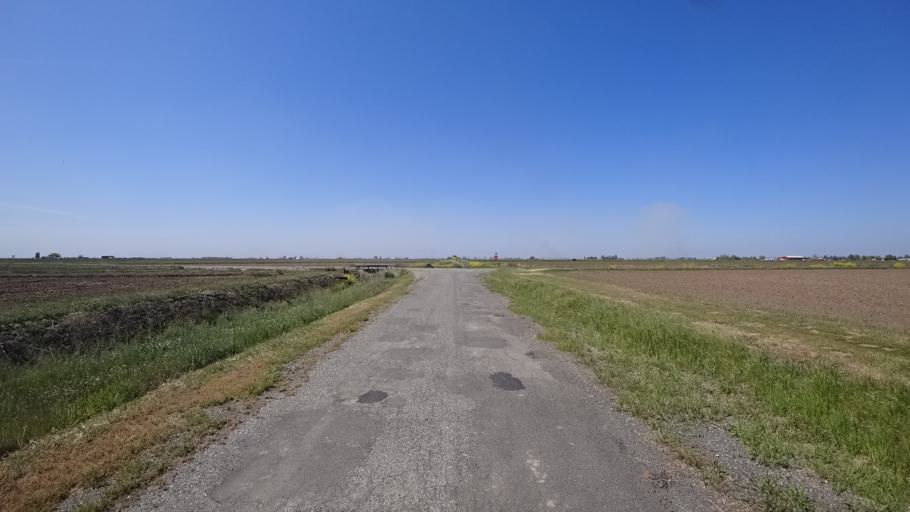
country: US
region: California
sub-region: Glenn County
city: Willows
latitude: 39.5653
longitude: -122.0267
